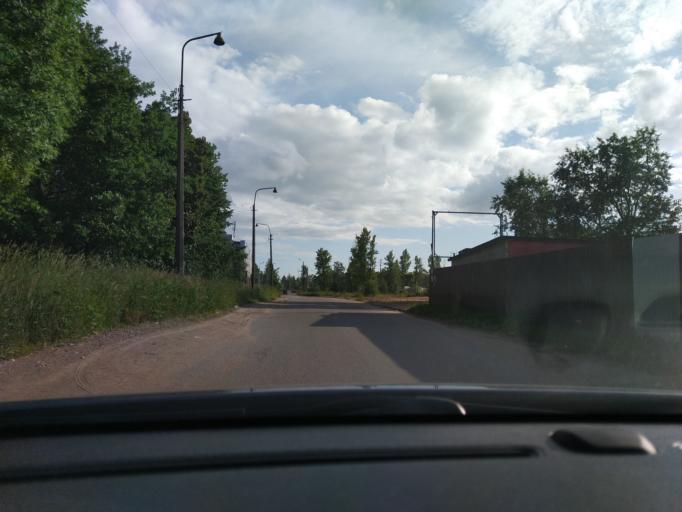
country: RU
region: St.-Petersburg
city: Gorelovo
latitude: 59.7820
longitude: 30.1512
